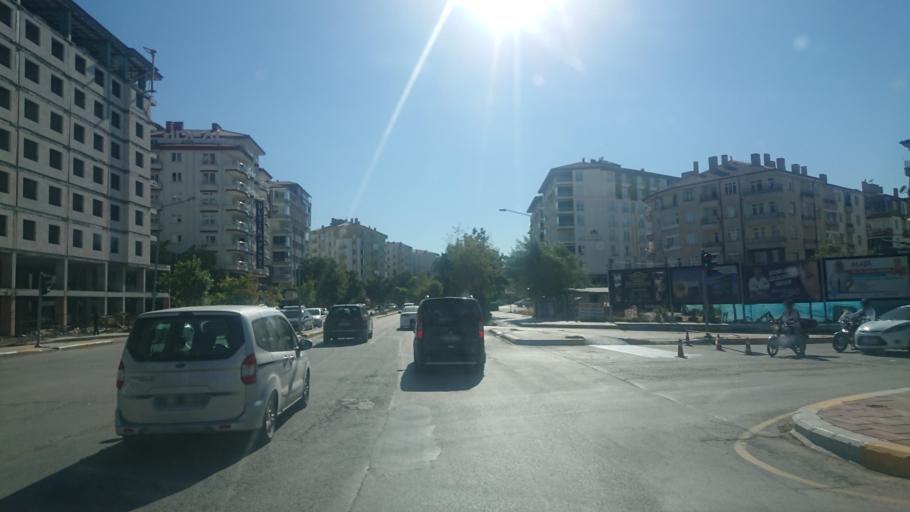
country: TR
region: Aksaray
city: Aksaray
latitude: 38.3647
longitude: 34.0204
